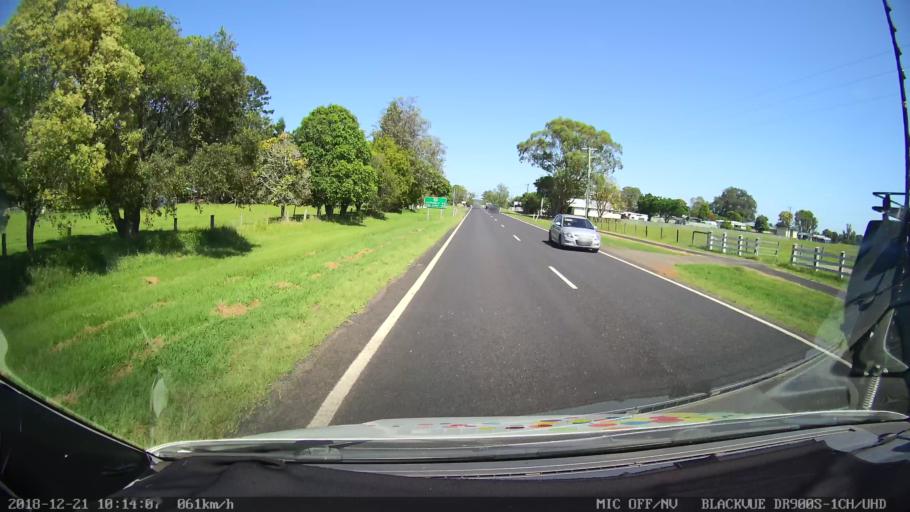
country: AU
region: New South Wales
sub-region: Clarence Valley
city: South Grafton
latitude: -29.6964
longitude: 152.9161
